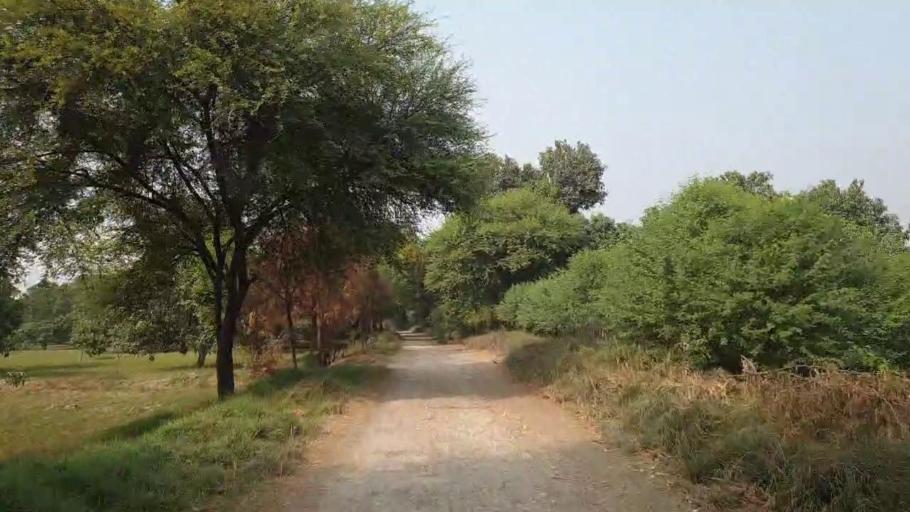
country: PK
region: Sindh
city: Tando Muhammad Khan
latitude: 25.2102
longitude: 68.5589
